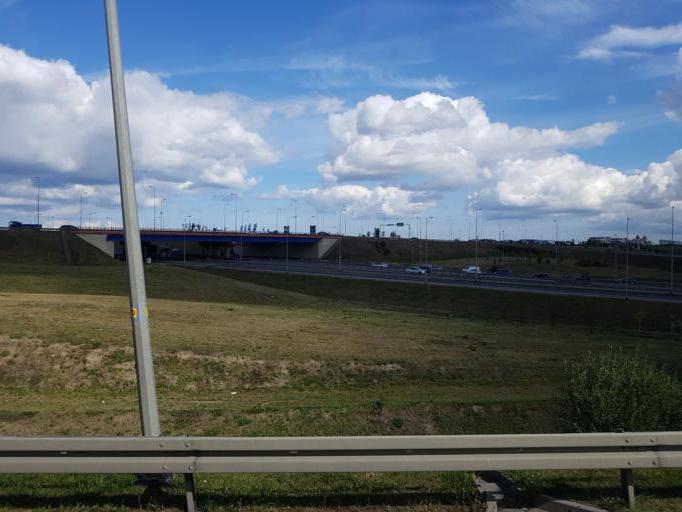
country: PL
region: Pomeranian Voivodeship
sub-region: Powiat gdanski
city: Kowale
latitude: 54.3482
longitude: 18.5170
